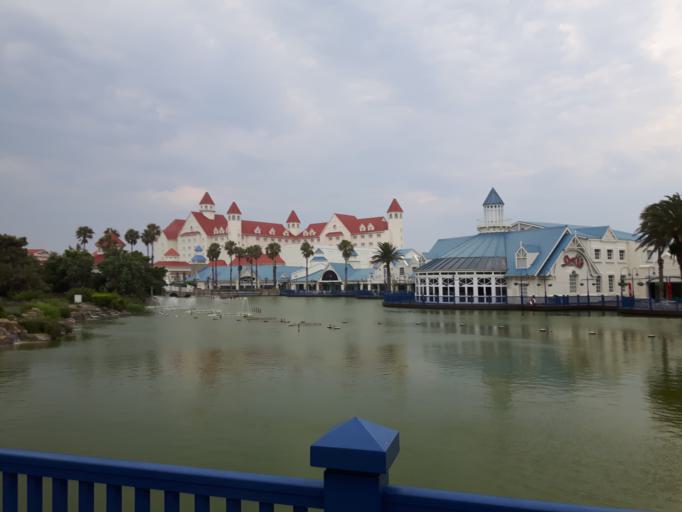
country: ZA
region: Eastern Cape
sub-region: Nelson Mandela Bay Metropolitan Municipality
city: Port Elizabeth
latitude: -33.9842
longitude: 25.6585
